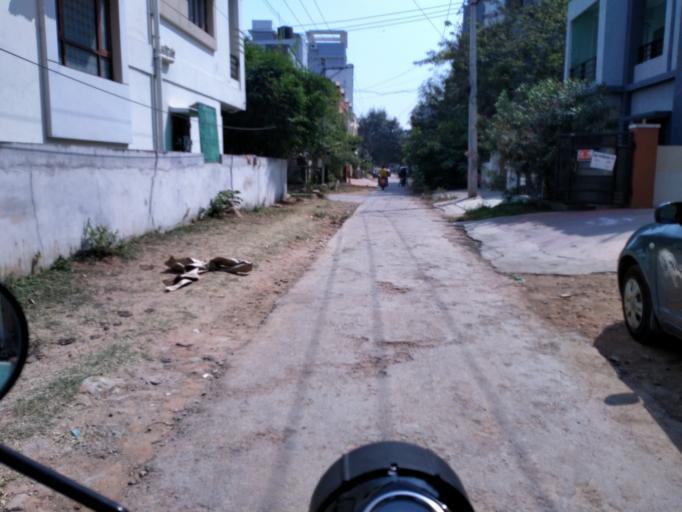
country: IN
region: Telangana
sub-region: Rangareddi
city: Secunderabad
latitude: 17.4962
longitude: 78.5454
